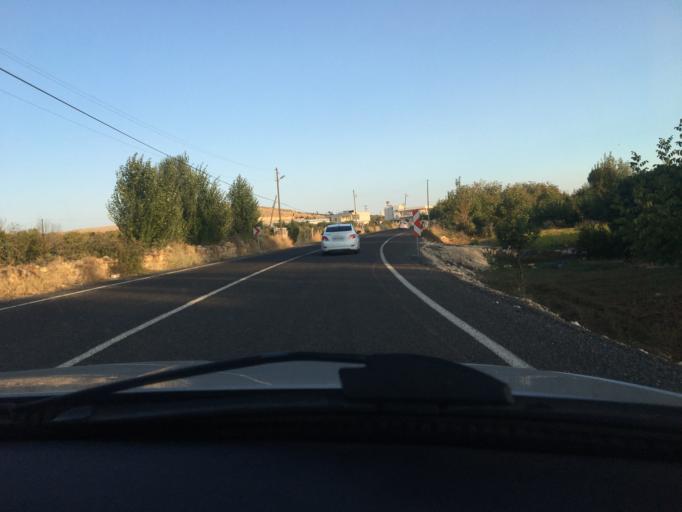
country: TR
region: Sanliurfa
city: Halfeti
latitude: 37.2085
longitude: 37.9677
